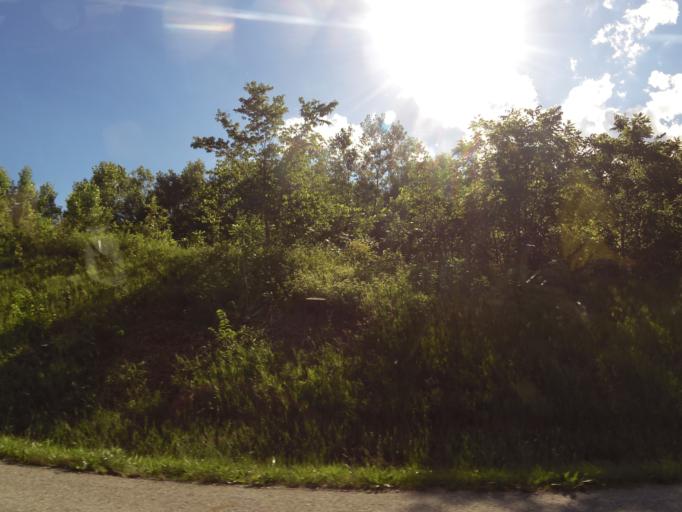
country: US
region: Missouri
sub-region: Marion County
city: Palmyra
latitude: 39.7558
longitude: -91.5189
